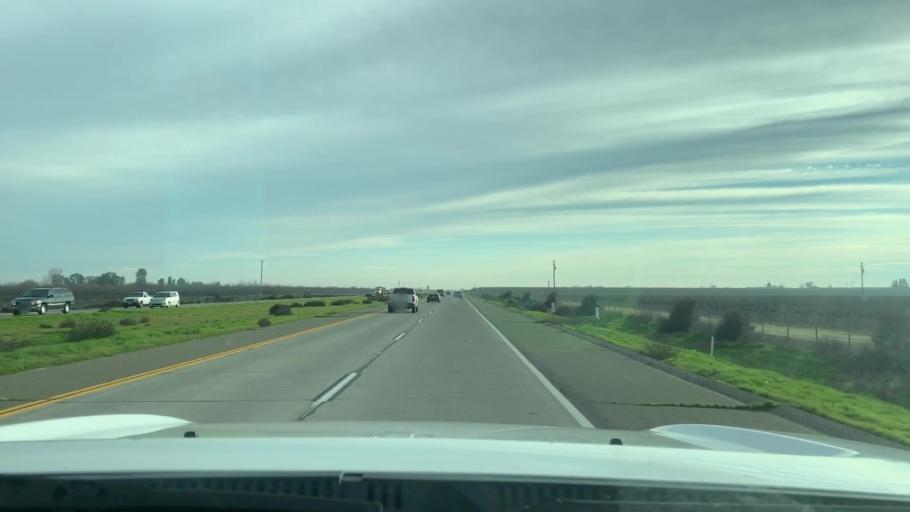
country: US
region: California
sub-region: Fresno County
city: Caruthers
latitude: 36.5387
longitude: -119.7864
